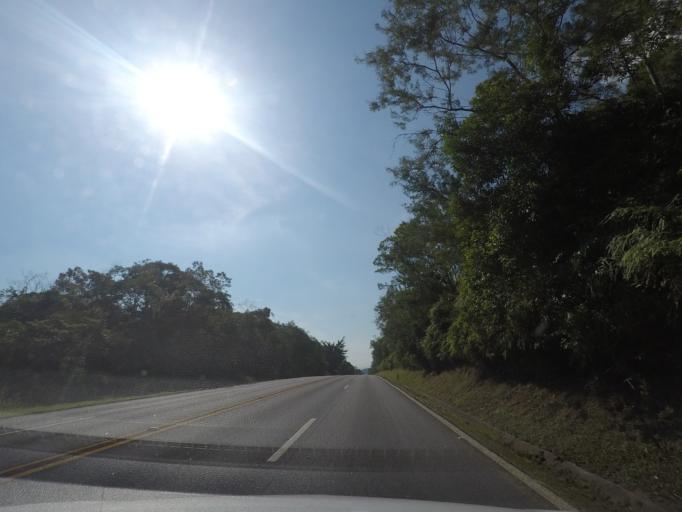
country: BR
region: Parana
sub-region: Paranagua
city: Paranagua
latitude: -25.5963
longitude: -48.6105
